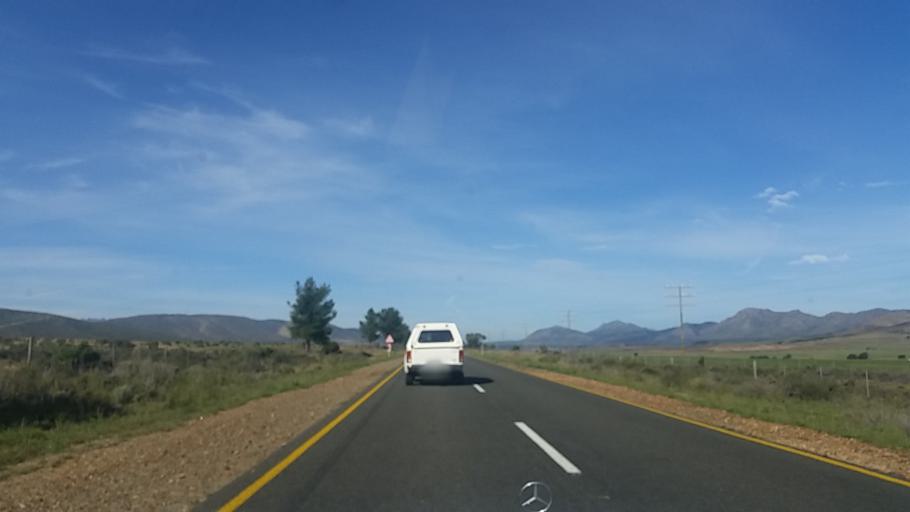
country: ZA
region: Western Cape
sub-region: Eden District Municipality
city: George
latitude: -33.8185
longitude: 22.5034
